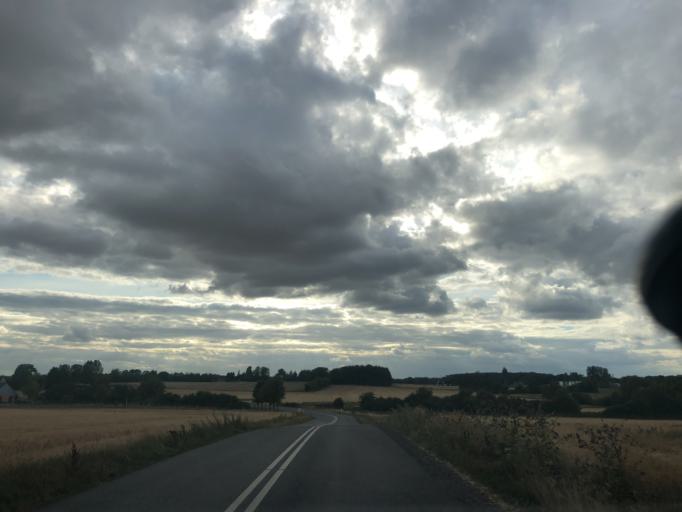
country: DK
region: Zealand
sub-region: Koge Kommune
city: Bjaeverskov
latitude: 55.4060
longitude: 12.0653
